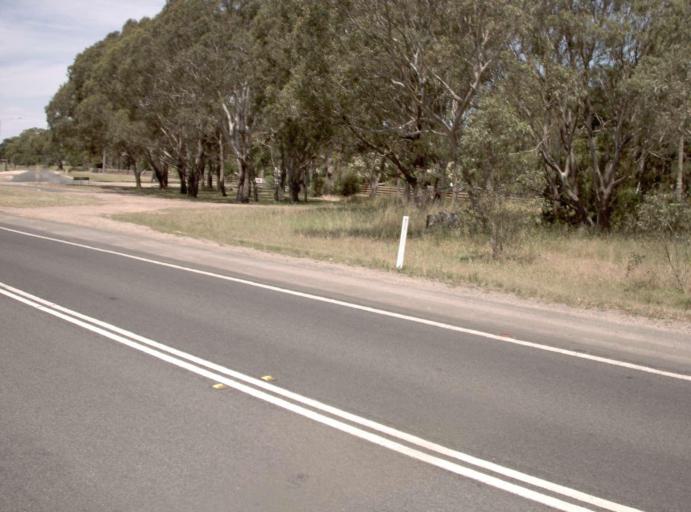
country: AU
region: Victoria
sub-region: Wellington
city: Heyfield
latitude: -38.1551
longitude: 146.7631
